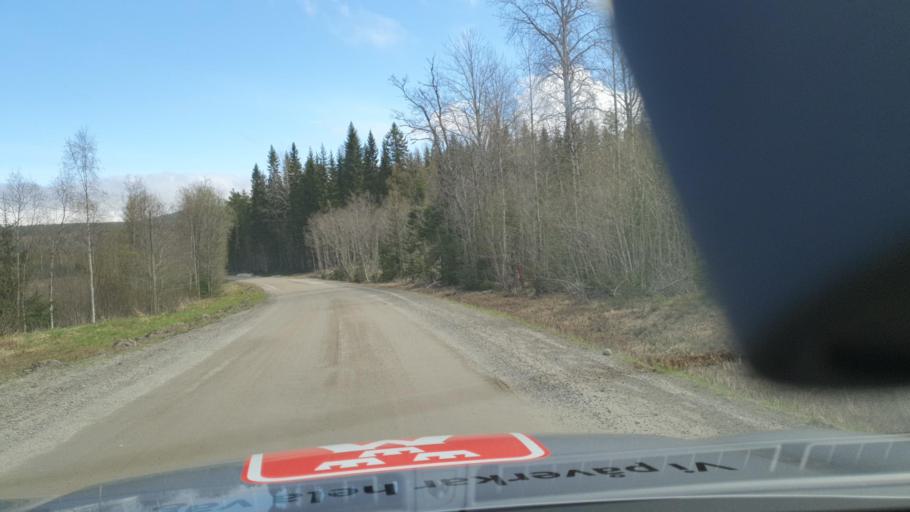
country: SE
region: Vaesterbotten
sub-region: Bjurholms Kommun
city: Bjurholm
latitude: 63.7014
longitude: 18.9264
